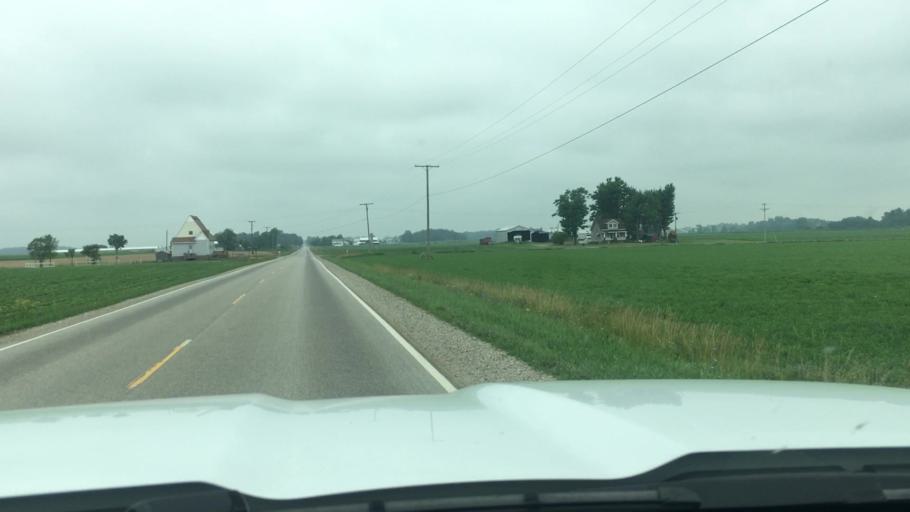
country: US
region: Michigan
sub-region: Sanilac County
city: Brown City
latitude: 43.2833
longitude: -82.9827
